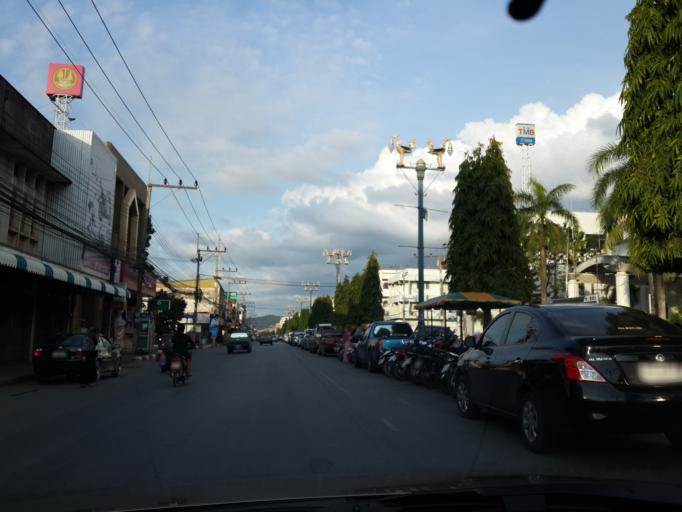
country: TH
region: Yala
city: Yala
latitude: 6.5564
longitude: 101.2863
